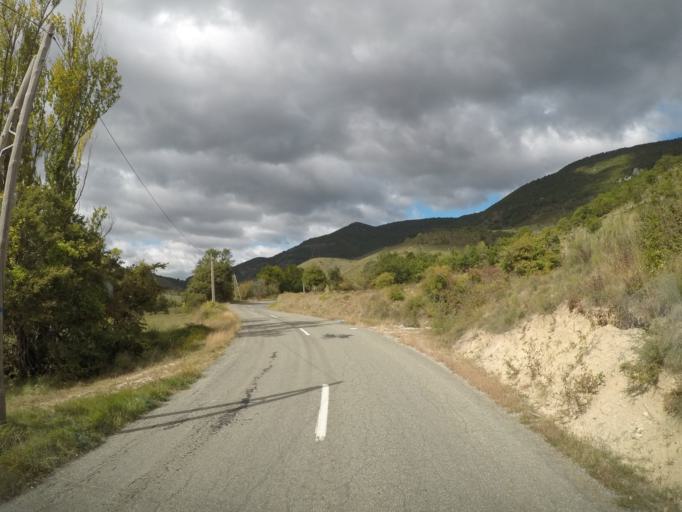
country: FR
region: Provence-Alpes-Cote d'Azur
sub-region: Departement du Vaucluse
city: Sault
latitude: 44.1740
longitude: 5.5928
